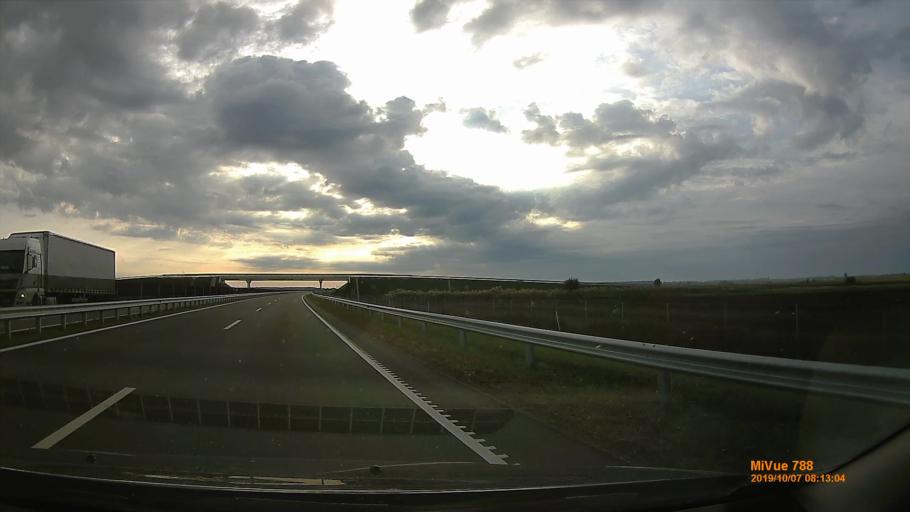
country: HU
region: Jasz-Nagykun-Szolnok
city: Cserkeszolo
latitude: 46.8816
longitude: 20.2364
